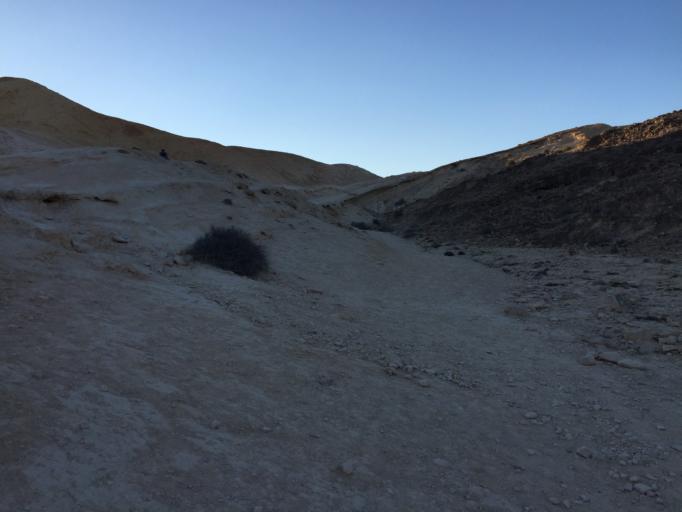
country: IL
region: Southern District
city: Midreshet Ben-Gurion
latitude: 30.8440
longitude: 34.7581
